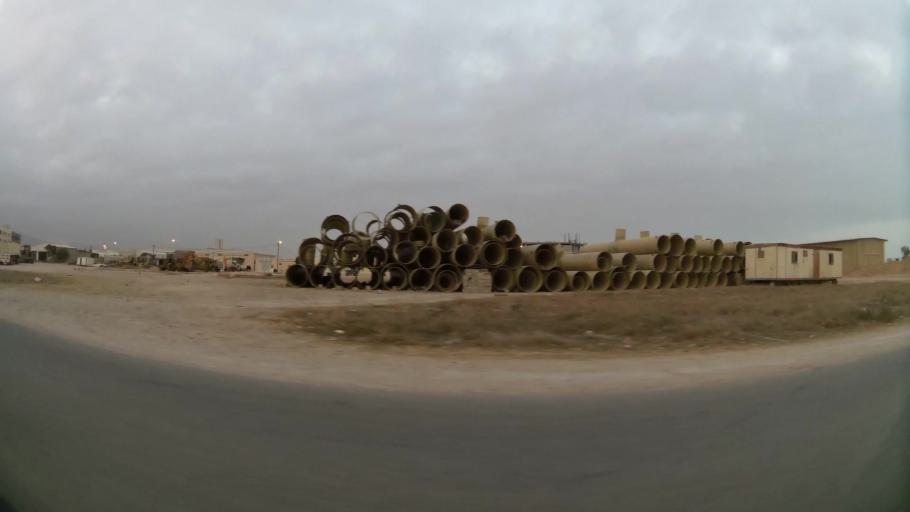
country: OM
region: Zufar
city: Salalah
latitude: 17.0273
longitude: 54.0335
